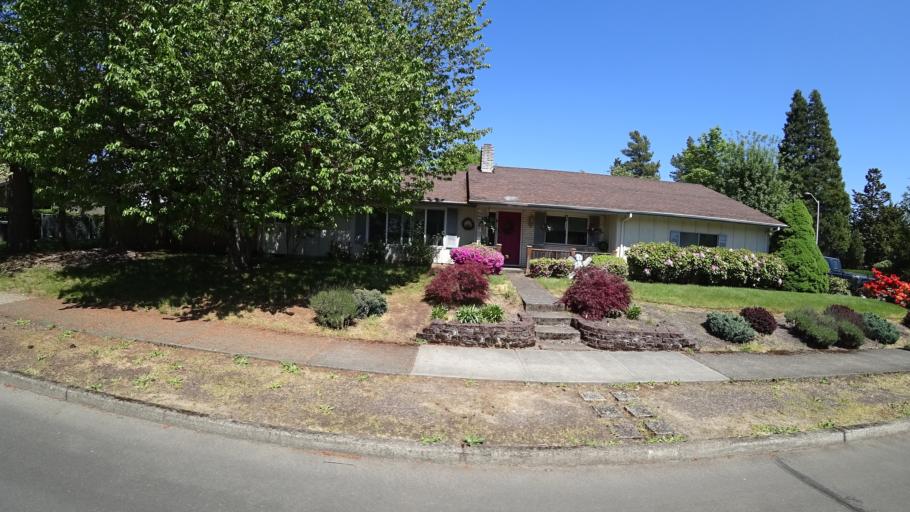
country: US
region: Oregon
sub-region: Washington County
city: Hillsboro
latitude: 45.5000
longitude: -122.9567
